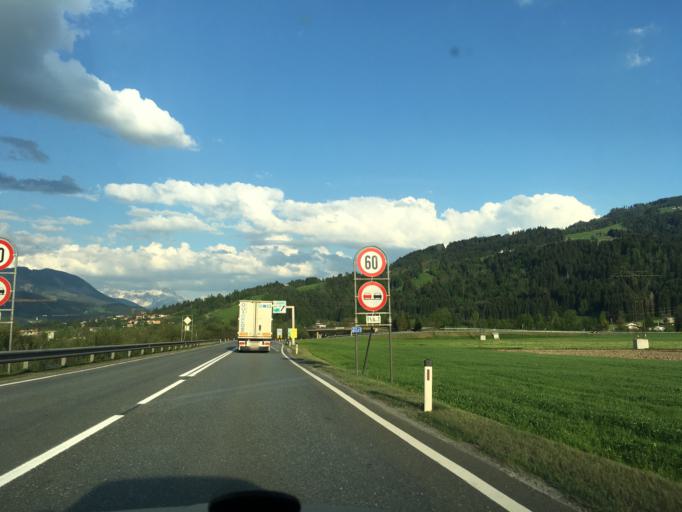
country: AT
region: Tyrol
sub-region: Politischer Bezirk Kitzbuhel
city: Sankt Johann in Tirol
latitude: 47.5184
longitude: 12.4055
